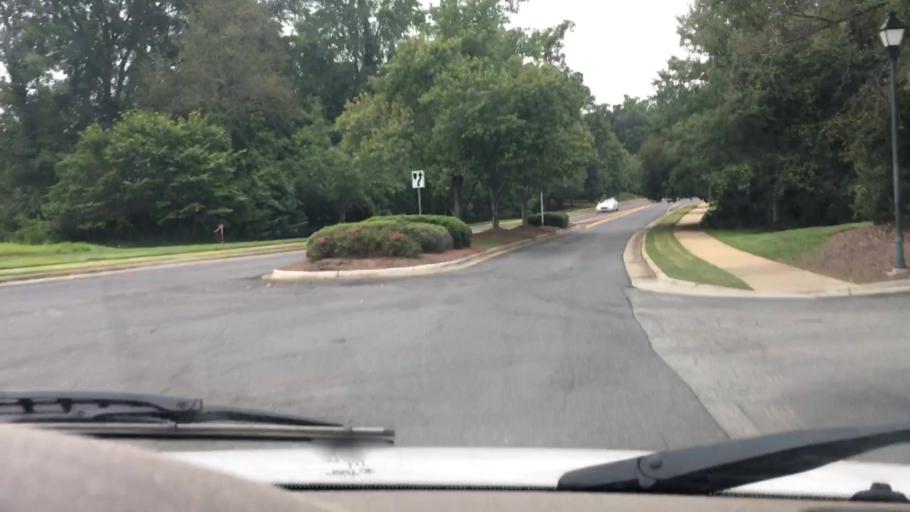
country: US
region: North Carolina
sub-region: Mecklenburg County
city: Huntersville
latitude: 35.4415
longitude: -80.8828
